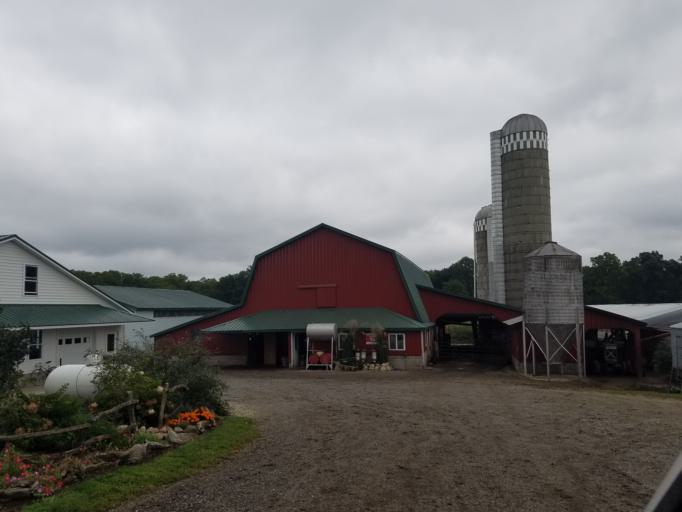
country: US
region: Indiana
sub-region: LaGrange County
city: Lagrange
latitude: 41.6794
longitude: -85.5024
